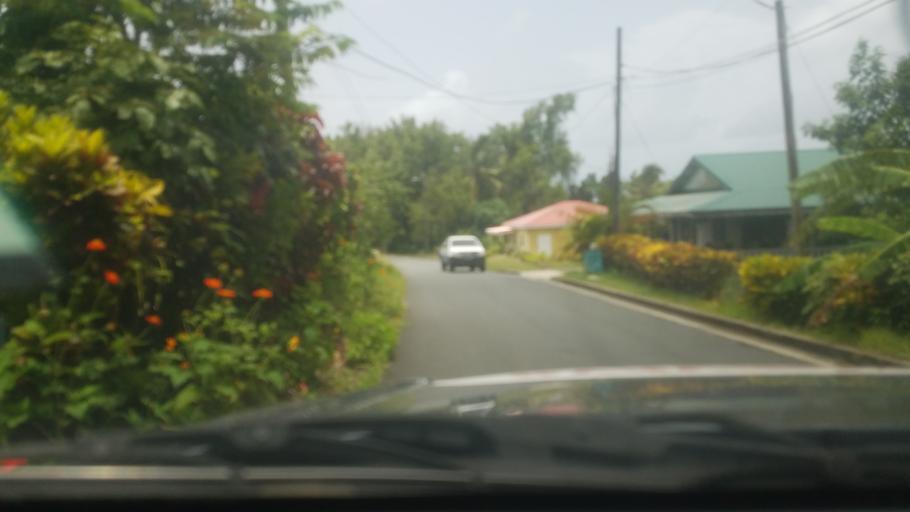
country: LC
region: Laborie Quarter
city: Laborie
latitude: 13.7684
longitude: -60.9889
